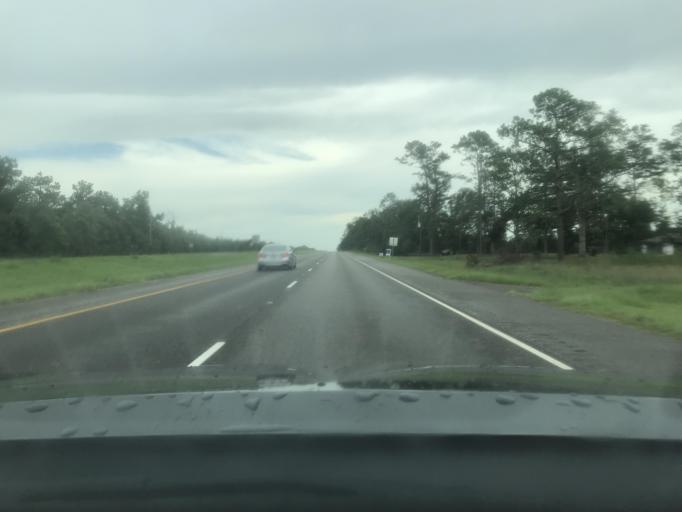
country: US
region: Louisiana
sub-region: Calcasieu Parish
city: Moss Bluff
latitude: 30.3933
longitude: -93.2261
